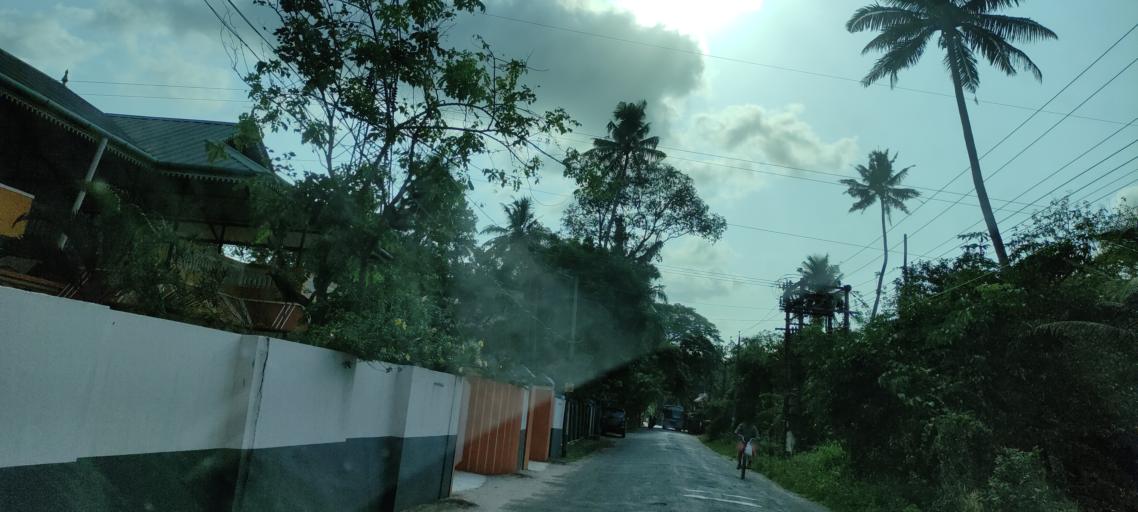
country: IN
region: Kerala
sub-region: Alappuzha
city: Vayalar
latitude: 9.6876
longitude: 76.3189
